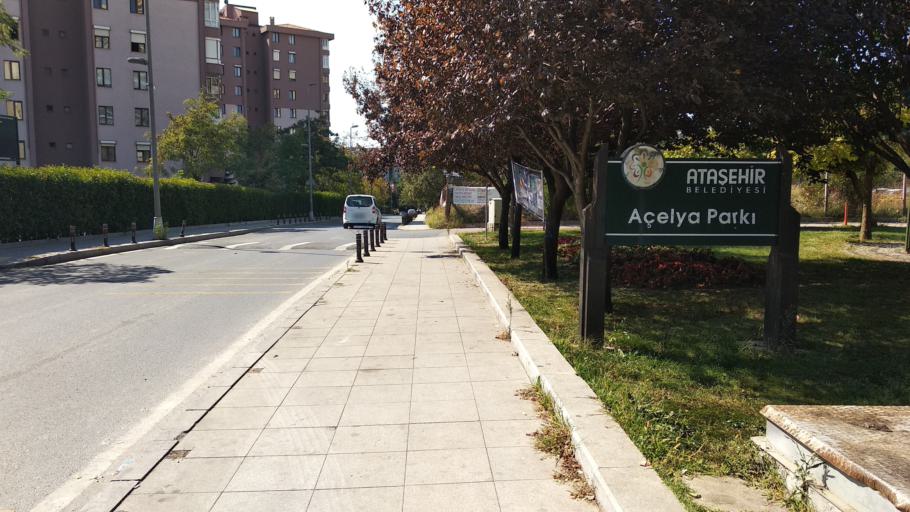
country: TR
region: Istanbul
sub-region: Atasehir
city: Atasehir
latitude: 41.0011
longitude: 29.0759
